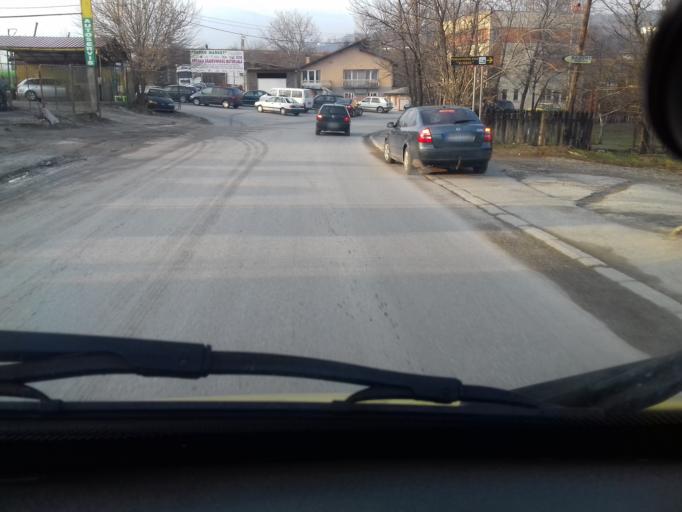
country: BA
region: Federation of Bosnia and Herzegovina
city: Kakanj
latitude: 44.1245
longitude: 18.1033
